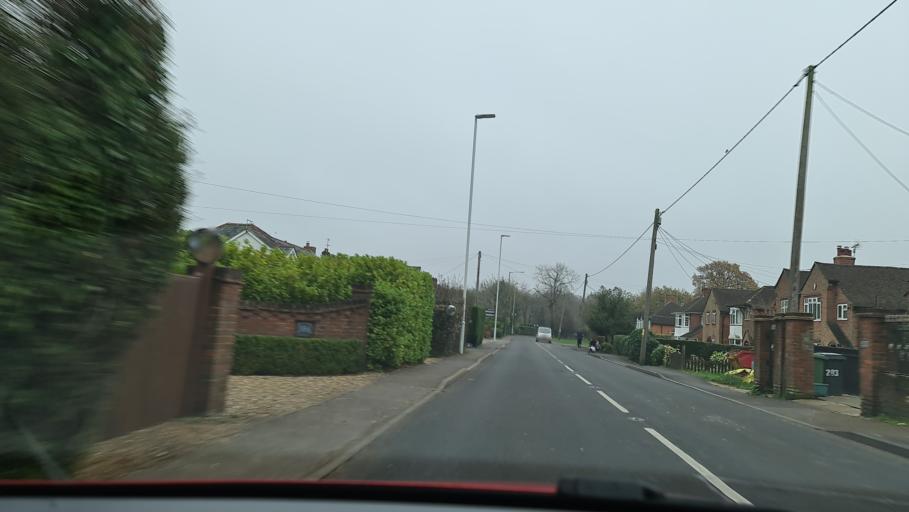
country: GB
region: England
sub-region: Buckinghamshire
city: High Wycombe
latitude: 51.6480
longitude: -0.6993
